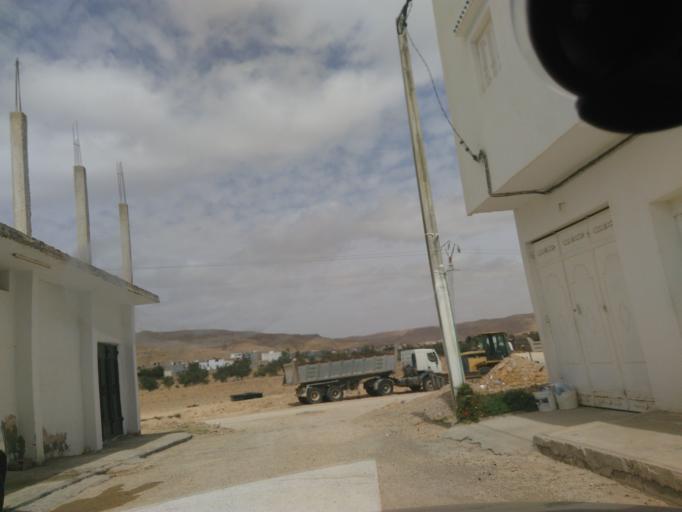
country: TN
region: Tataouine
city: Tataouine
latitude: 32.9520
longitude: 10.4643
